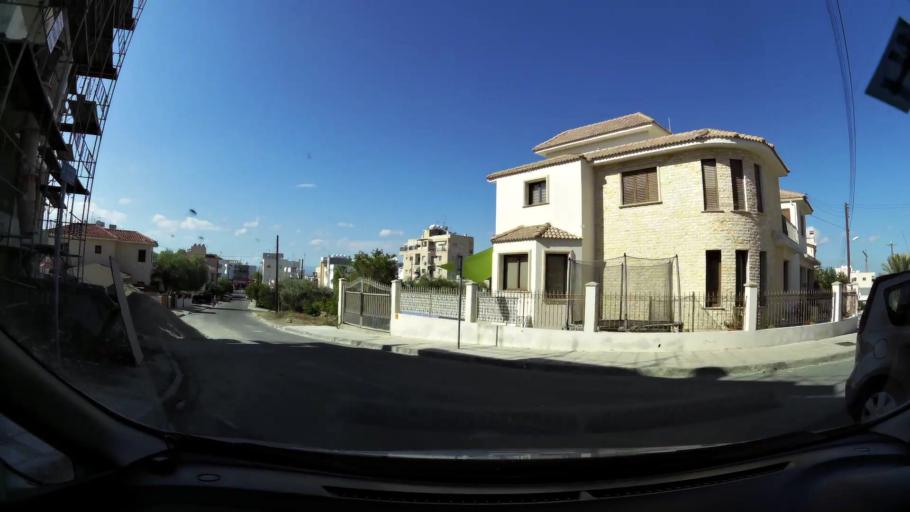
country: CY
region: Lefkosia
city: Nicosia
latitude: 35.1409
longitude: 33.3477
